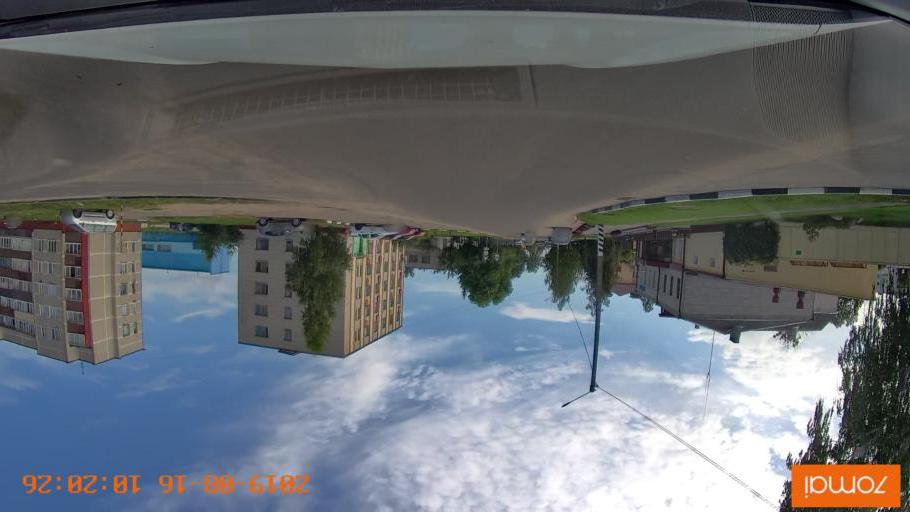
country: BY
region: Mogilev
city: Asipovichy
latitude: 53.3002
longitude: 28.6615
